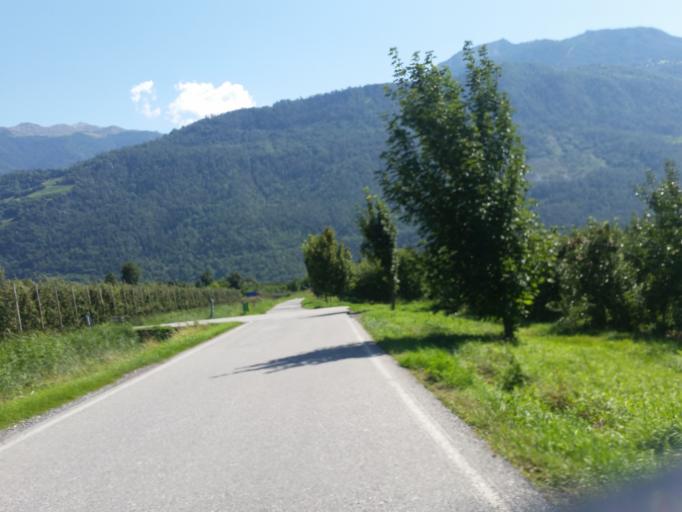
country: CH
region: Valais
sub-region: Conthey District
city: Vetroz
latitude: 46.2148
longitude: 7.2894
